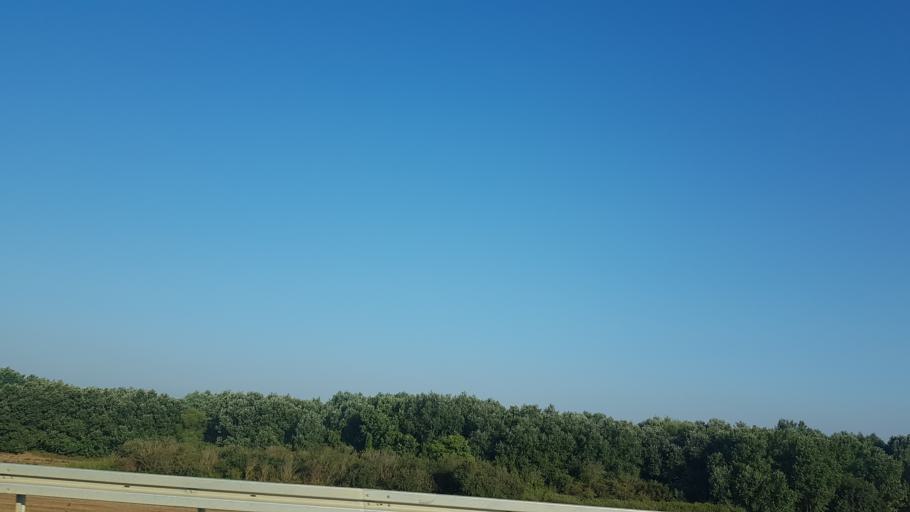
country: TR
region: Bursa
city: Karacabey
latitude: 40.1729
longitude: 28.3240
